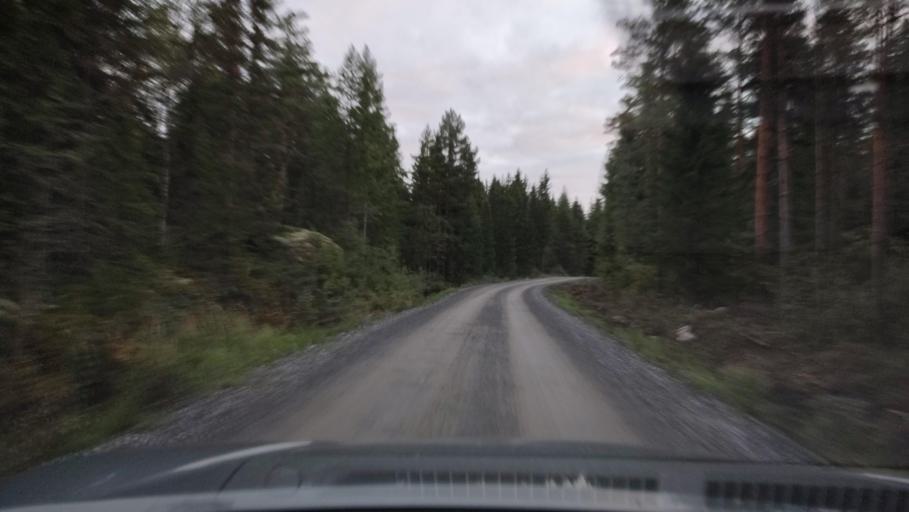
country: FI
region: Ostrobothnia
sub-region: Sydosterbotten
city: Kristinestad
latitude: 62.1922
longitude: 21.5425
